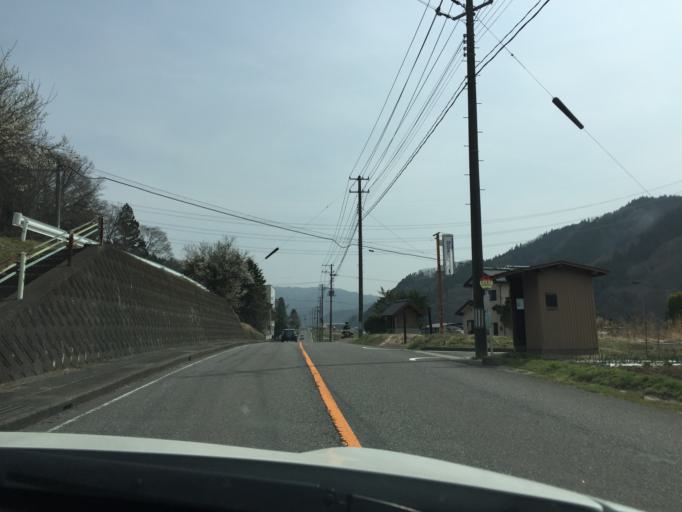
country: JP
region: Fukushima
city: Ishikawa
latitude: 37.1050
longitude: 140.5078
